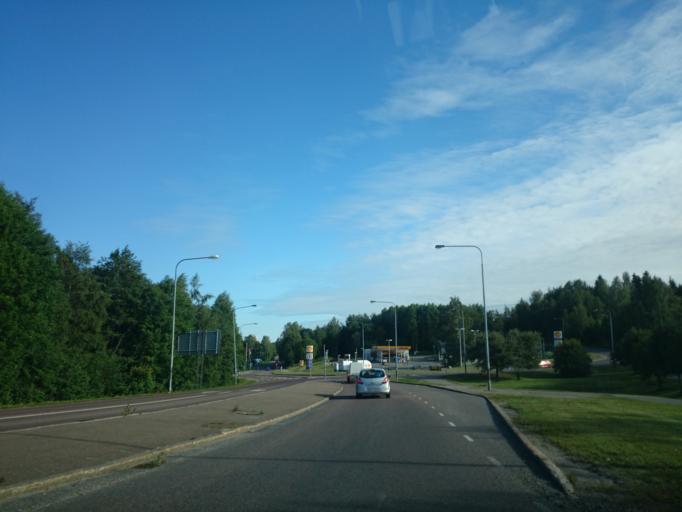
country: SE
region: Vaesternorrland
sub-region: Sundsvalls Kommun
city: Sundsvall
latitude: 62.4105
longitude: 17.3336
